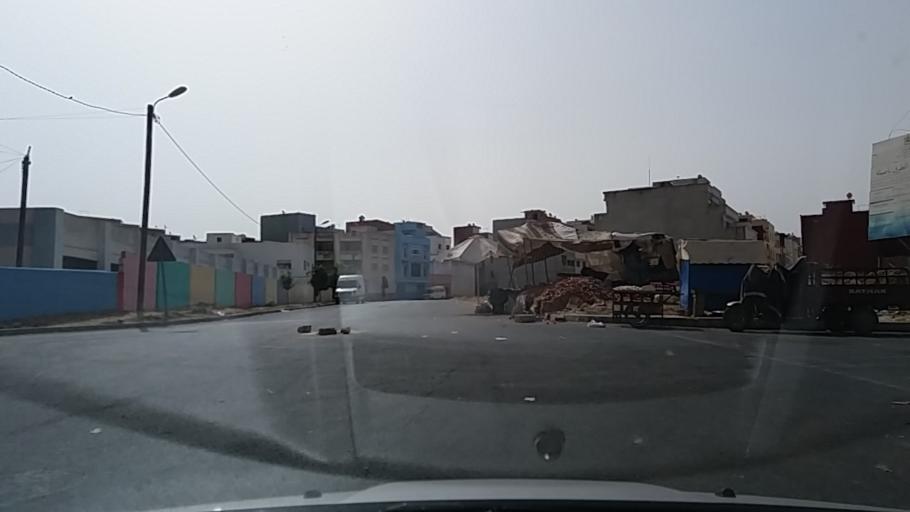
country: MA
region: Tanger-Tetouan
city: Asilah
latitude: 35.4606
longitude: -6.0399
